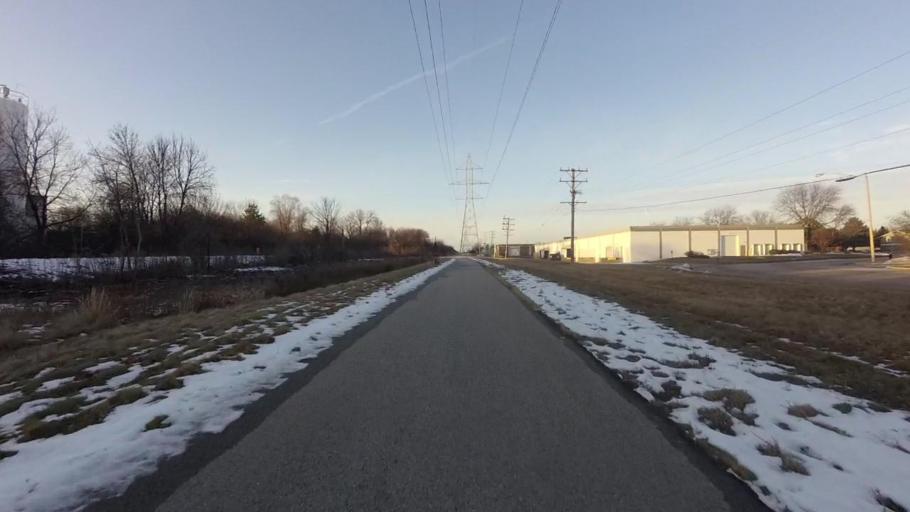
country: US
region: Wisconsin
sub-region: Milwaukee County
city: Glendale
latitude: 43.1351
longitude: -87.9487
